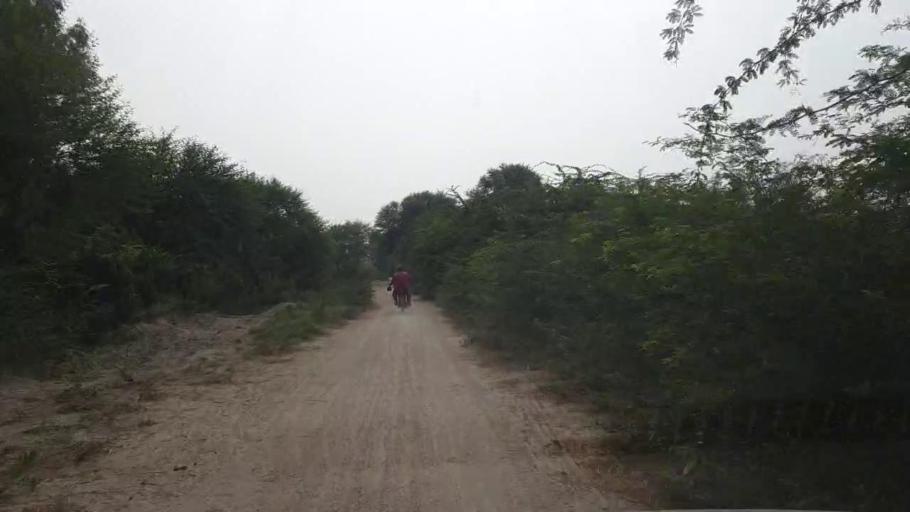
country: PK
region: Sindh
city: Matli
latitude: 24.9939
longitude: 68.7029
